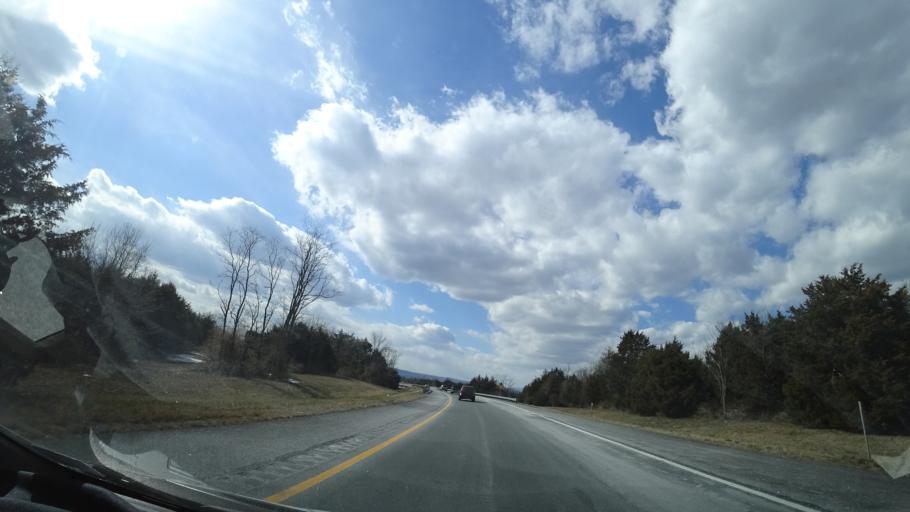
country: US
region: Virginia
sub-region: Frederick County
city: Middletown
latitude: 39.0093
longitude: -78.2954
